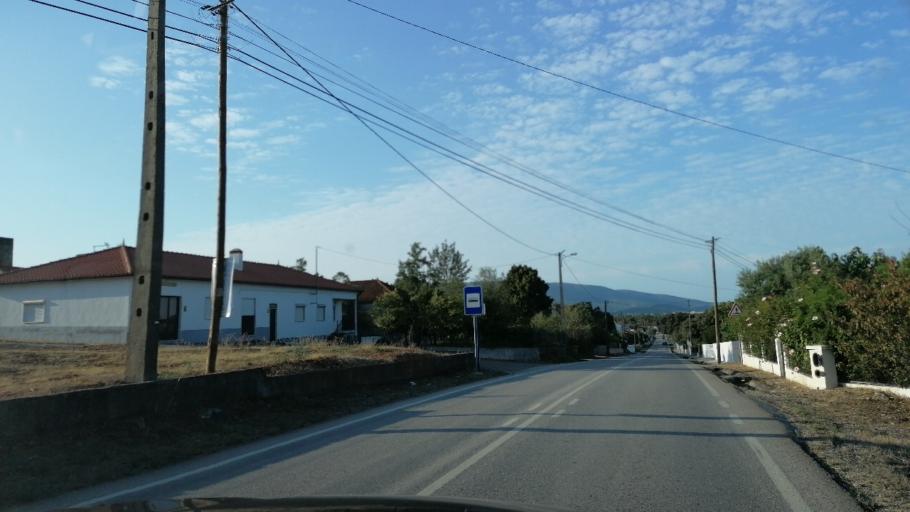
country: PT
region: Santarem
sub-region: Alcanena
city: Alcanena
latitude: 39.4461
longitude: -8.6233
